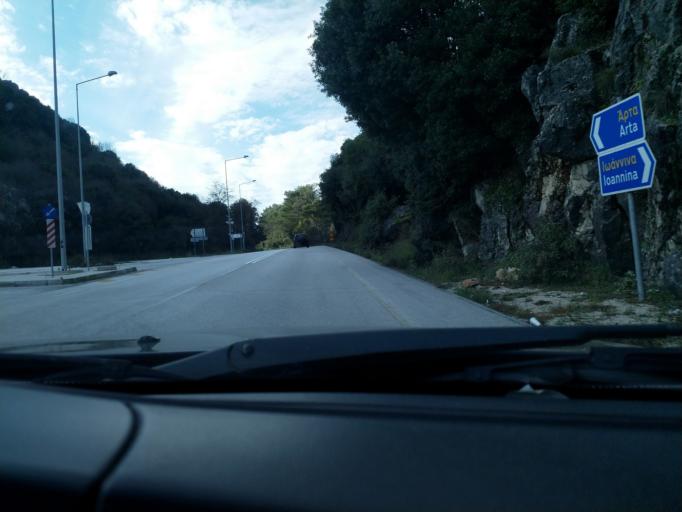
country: GR
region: Epirus
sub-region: Nomos Ioanninon
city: Agia Kyriaki
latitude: 39.5027
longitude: 20.8822
